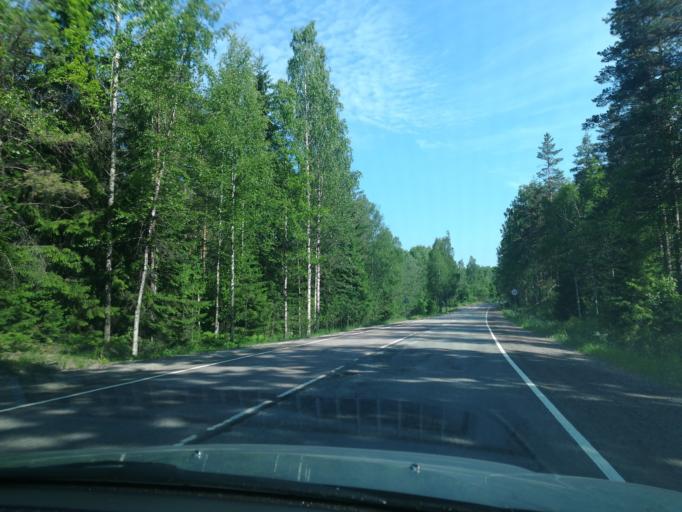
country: RU
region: Leningrad
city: Lesogorskiy
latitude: 60.9073
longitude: 28.8732
